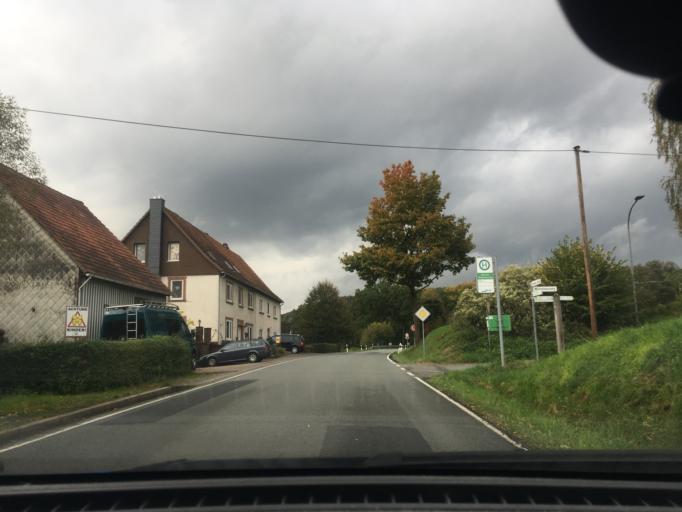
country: DE
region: Lower Saxony
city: Bodenfelde
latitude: 51.6825
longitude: 9.5268
